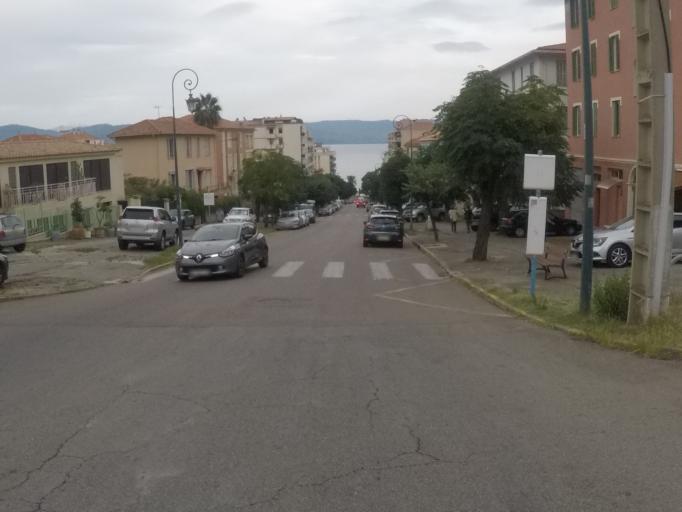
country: FR
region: Corsica
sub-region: Departement de la Corse-du-Sud
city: Ajaccio
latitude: 41.9157
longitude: 8.7240
